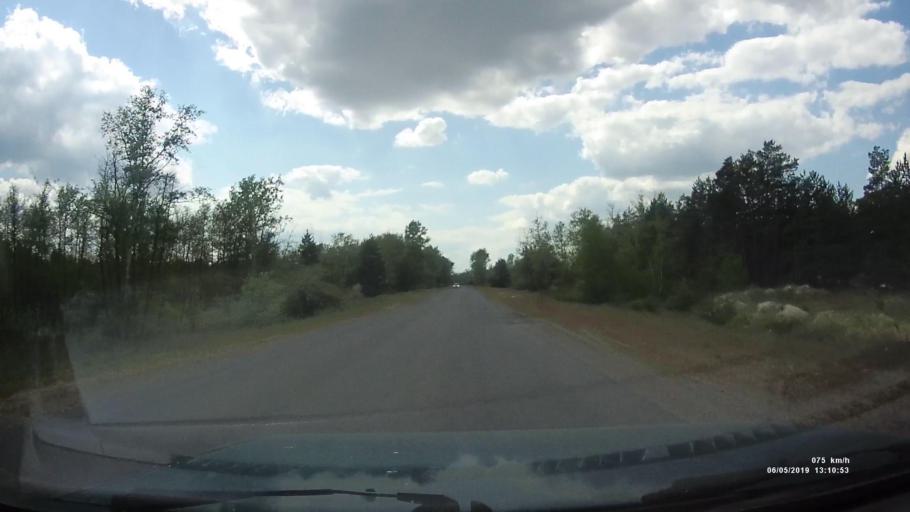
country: RU
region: Rostov
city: Ust'-Donetskiy
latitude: 47.7589
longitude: 40.9649
